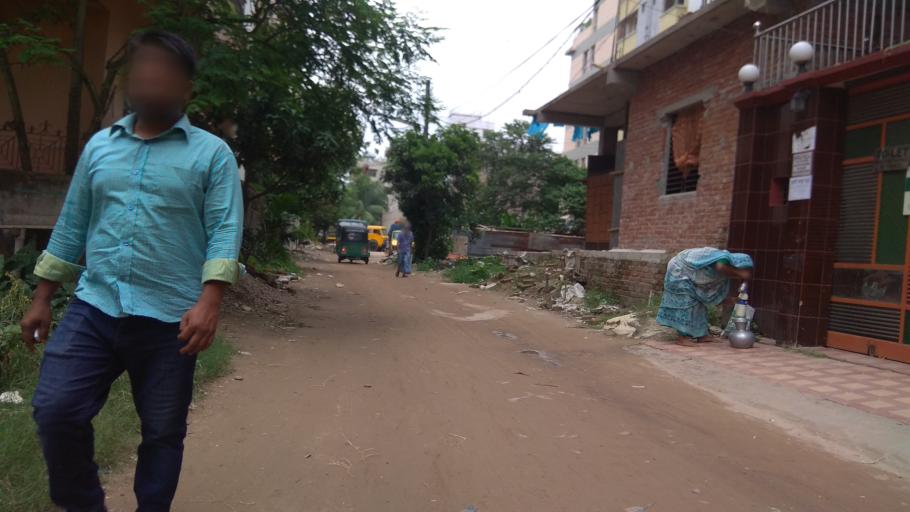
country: BD
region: Dhaka
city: Tungi
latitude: 23.8228
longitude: 90.3525
